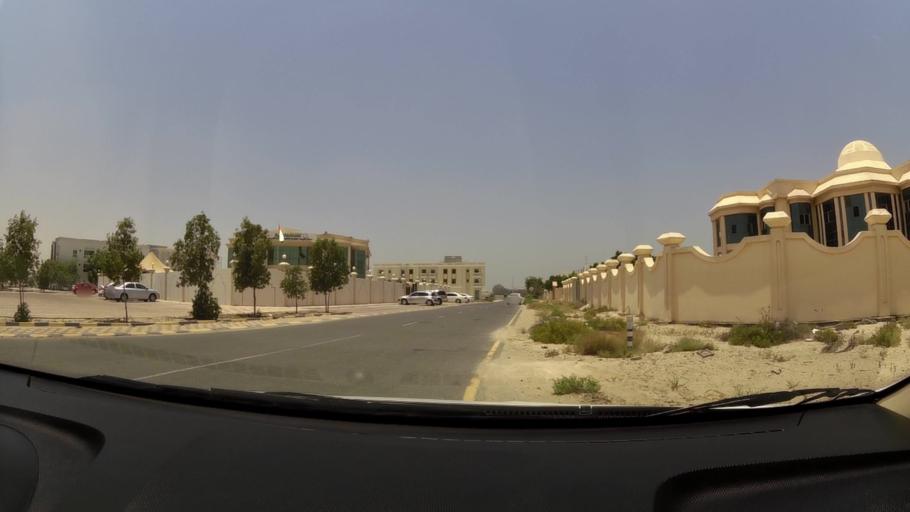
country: AE
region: Umm al Qaywayn
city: Umm al Qaywayn
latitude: 25.5322
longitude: 55.5410
